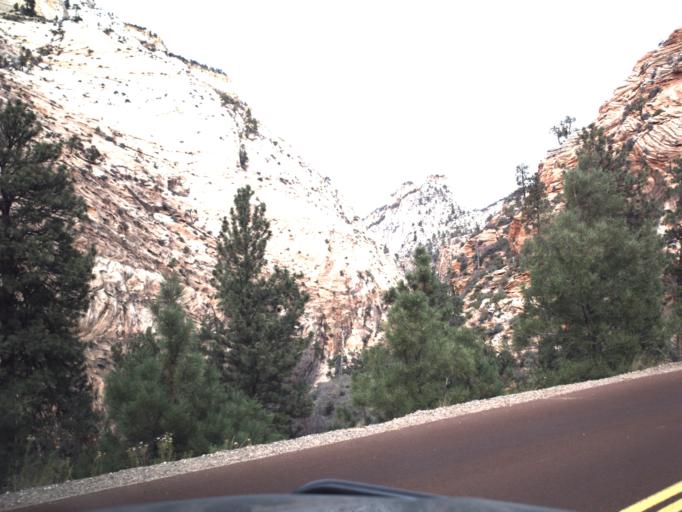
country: US
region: Utah
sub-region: Washington County
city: Hildale
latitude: 37.2213
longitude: -112.9170
